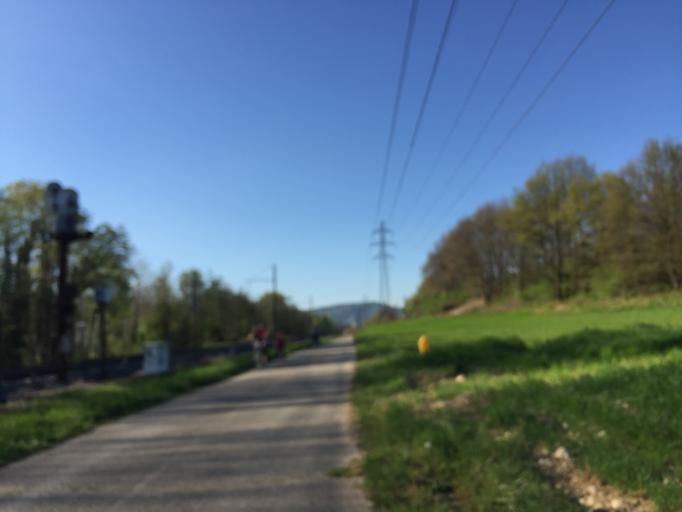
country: FR
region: Rhone-Alpes
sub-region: Departement de la Savoie
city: Saint-Baldoph
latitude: 45.5407
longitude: 5.9630
